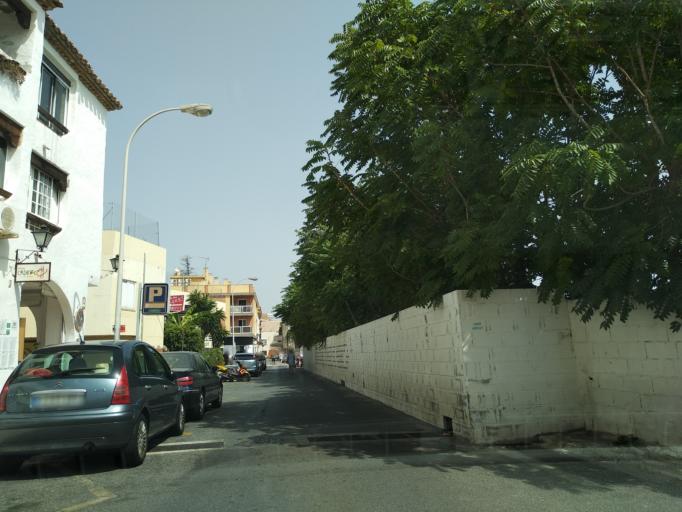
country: ES
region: Andalusia
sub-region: Provincia de Malaga
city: Torremolinos
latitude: 36.6204
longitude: -4.4977
